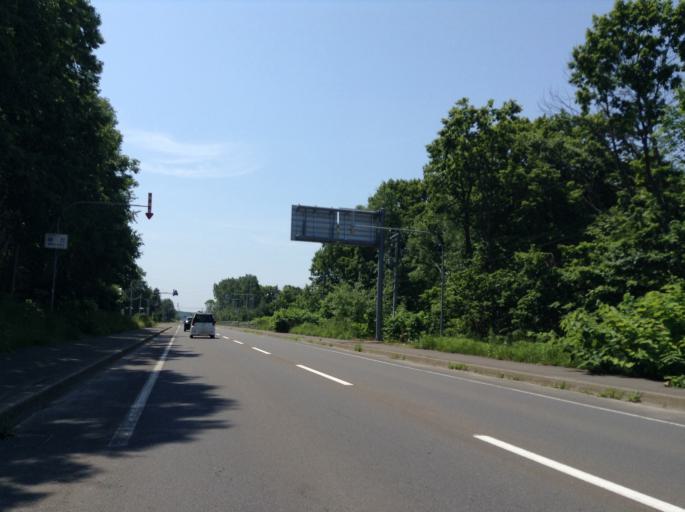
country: JP
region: Hokkaido
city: Nayoro
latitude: 44.3453
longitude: 142.4749
